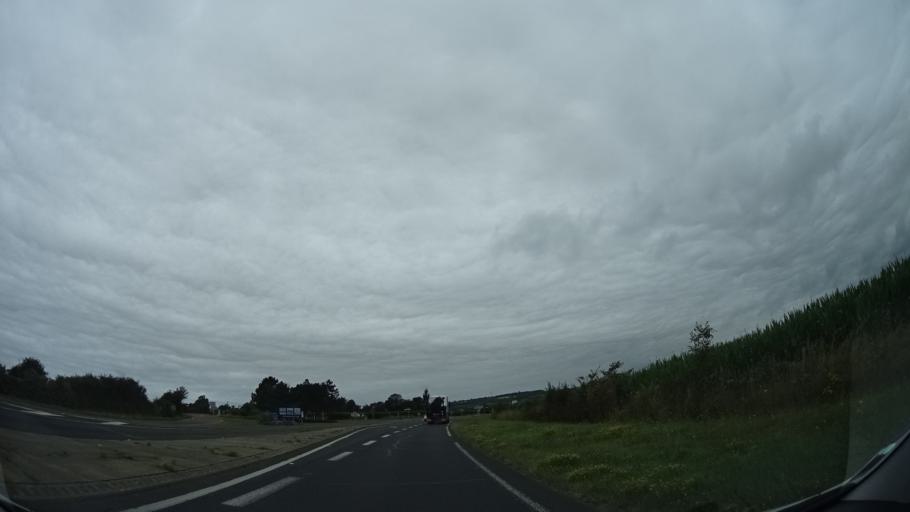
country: FR
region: Lower Normandy
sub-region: Departement de la Manche
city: Barneville-Plage
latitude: 49.3779
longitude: -1.7408
